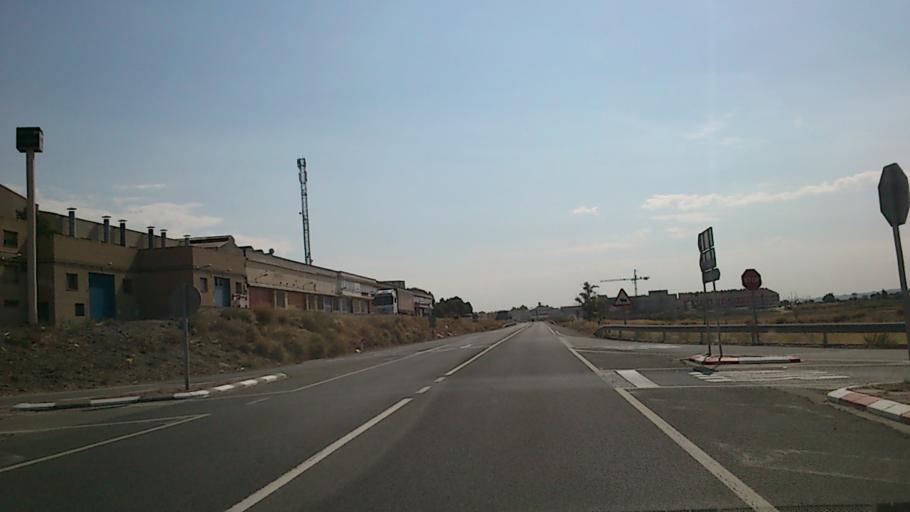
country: ES
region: Aragon
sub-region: Provincia de Zaragoza
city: Puebla de Alfinden
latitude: 41.6381
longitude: -0.7638
